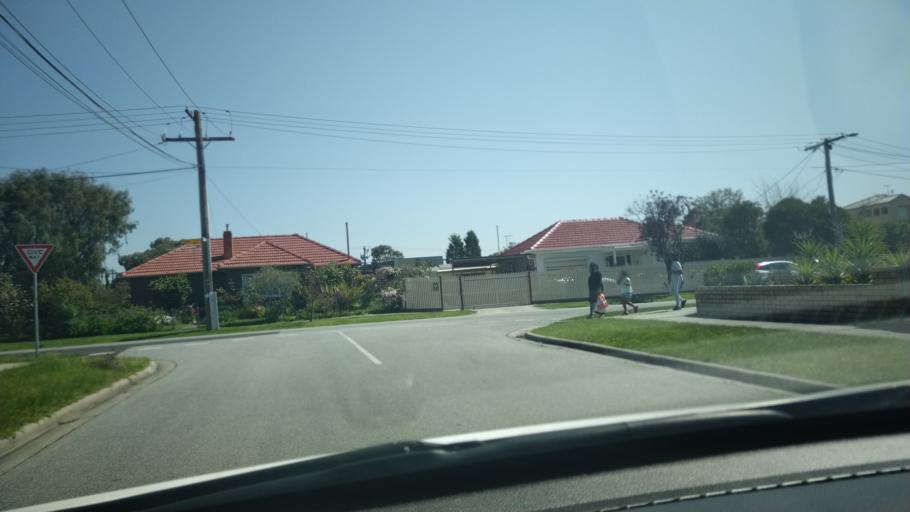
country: AU
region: Victoria
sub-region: Greater Dandenong
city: Noble Park
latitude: -37.9712
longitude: 145.1771
